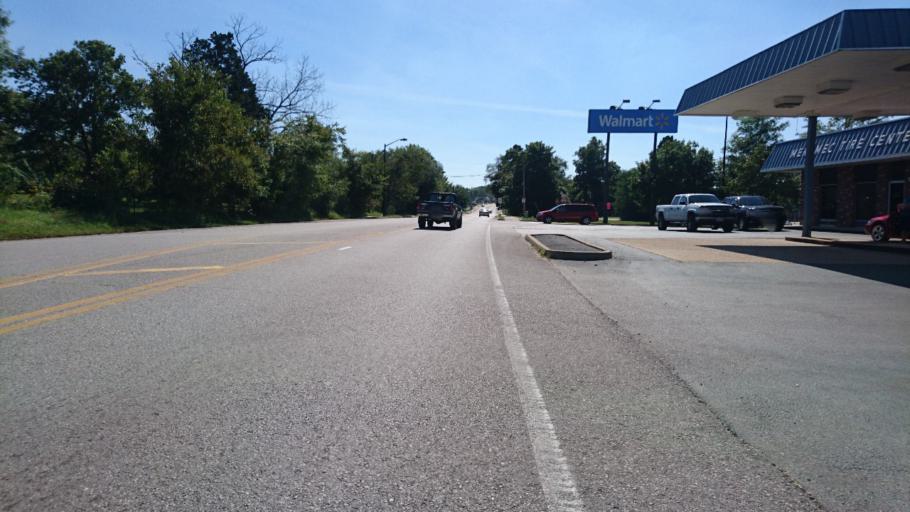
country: US
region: Missouri
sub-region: Franklin County
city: Sullivan
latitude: 38.2221
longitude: -91.1525
